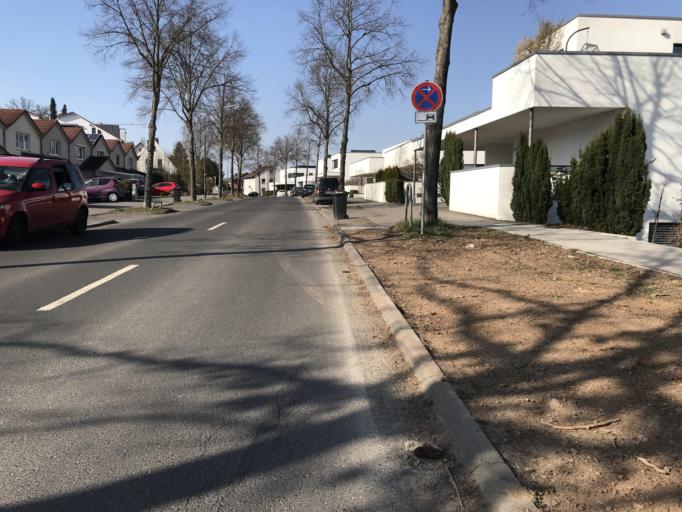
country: DE
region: Hesse
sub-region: Regierungsbezirk Kassel
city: Fulda
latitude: 50.5419
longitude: 9.6636
